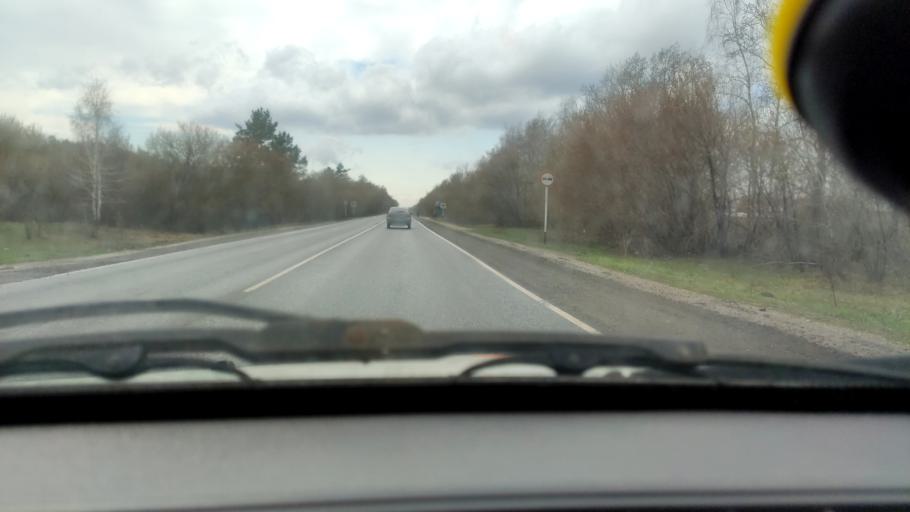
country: RU
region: Samara
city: Povolzhskiy
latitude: 53.6095
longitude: 49.6147
